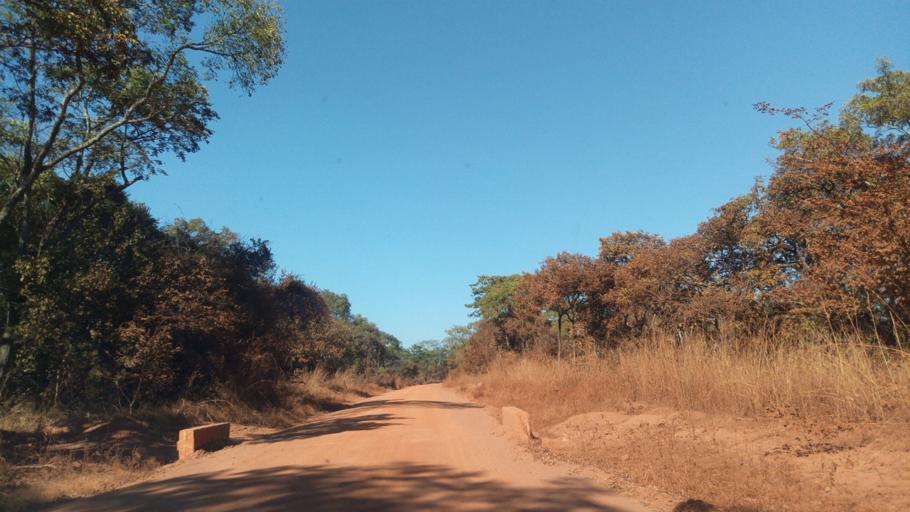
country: ZM
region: Luapula
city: Mwense
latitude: -10.7220
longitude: 28.3615
